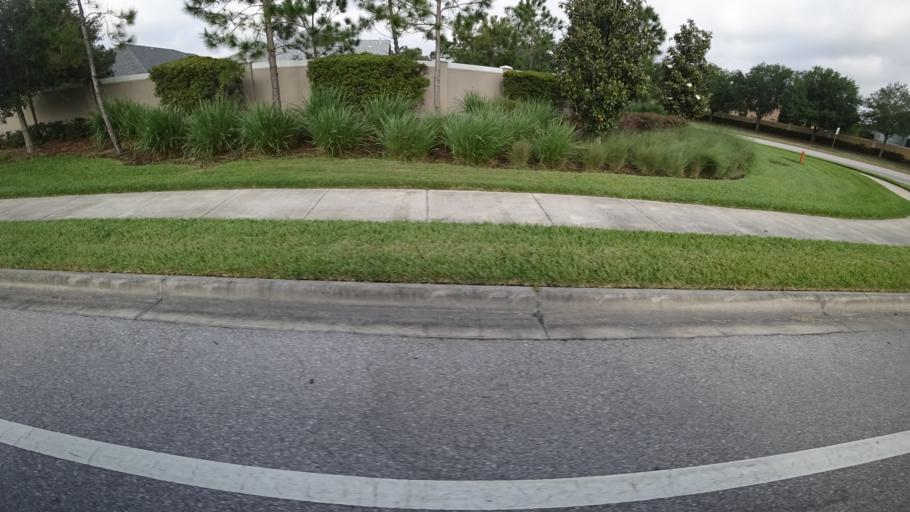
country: US
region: Florida
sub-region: Sarasota County
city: North Sarasota
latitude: 27.4193
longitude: -82.5134
